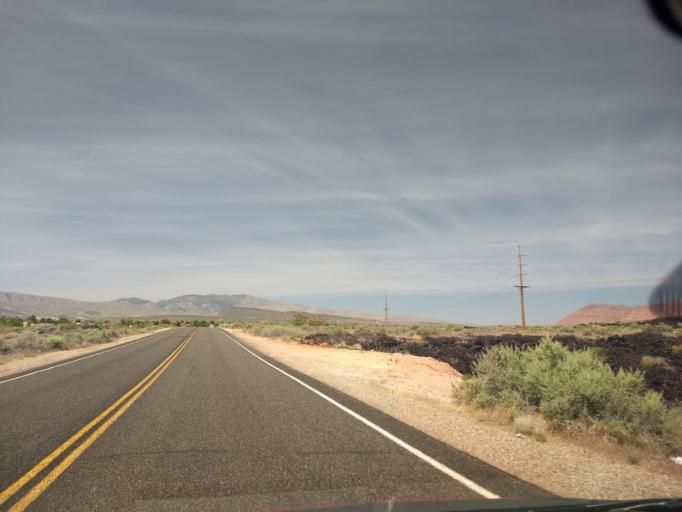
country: US
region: Utah
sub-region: Washington County
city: Santa Clara
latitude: 37.1440
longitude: -113.6475
